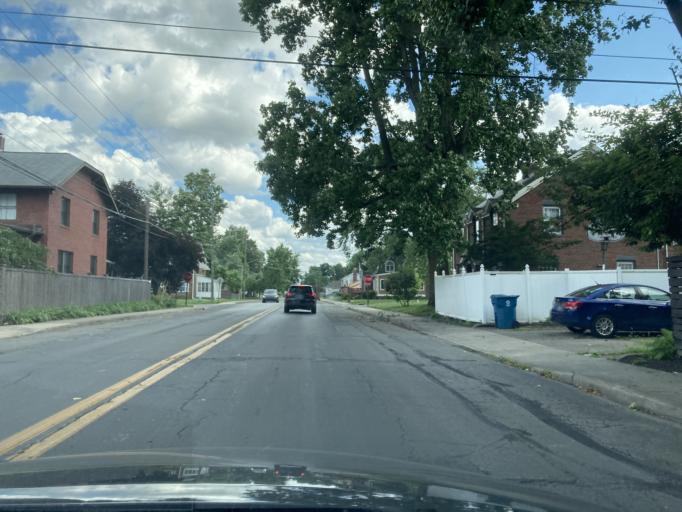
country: US
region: Indiana
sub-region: Marion County
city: Broad Ripple
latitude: 39.8372
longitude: -86.1641
